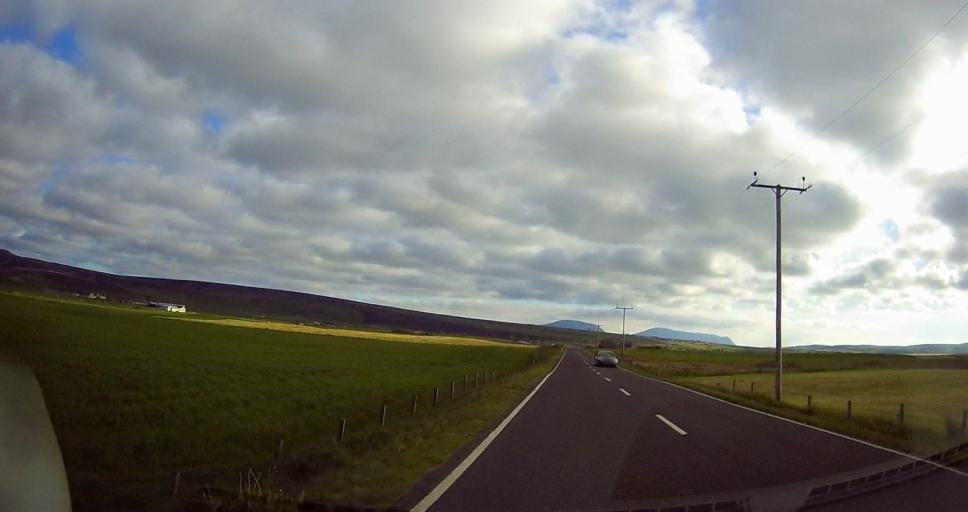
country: GB
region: Scotland
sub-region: Orkney Islands
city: Stromness
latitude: 58.9992
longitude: -3.1784
